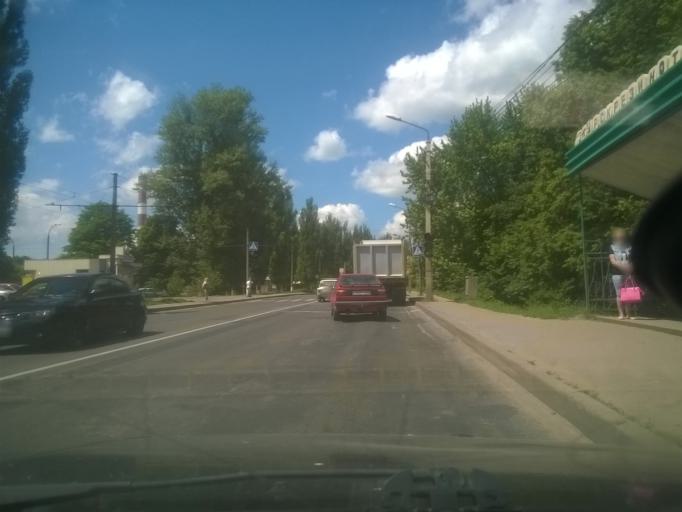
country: RU
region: Kursk
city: Kursk
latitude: 51.6618
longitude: 36.1252
